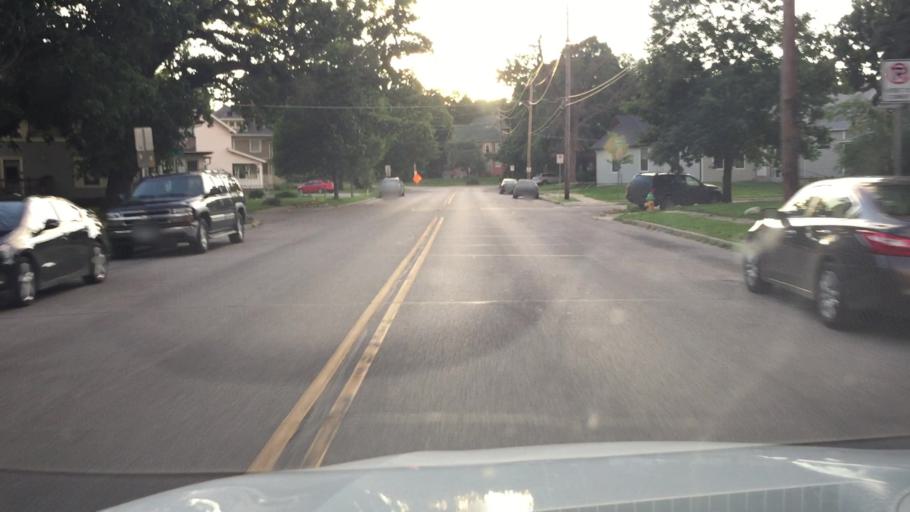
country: US
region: Iowa
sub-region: Polk County
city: Des Moines
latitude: 41.5980
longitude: -93.6530
